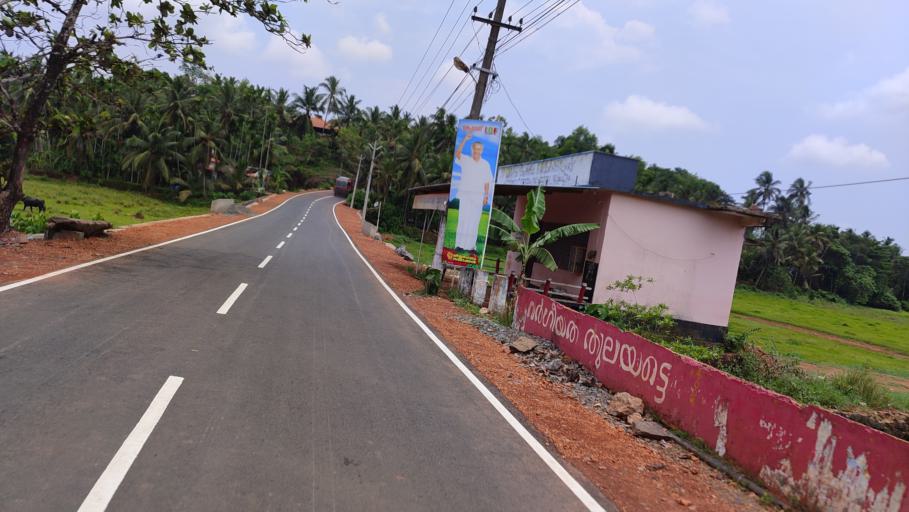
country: IN
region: Kerala
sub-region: Kasaragod District
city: Kannangad
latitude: 12.3171
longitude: 75.1376
